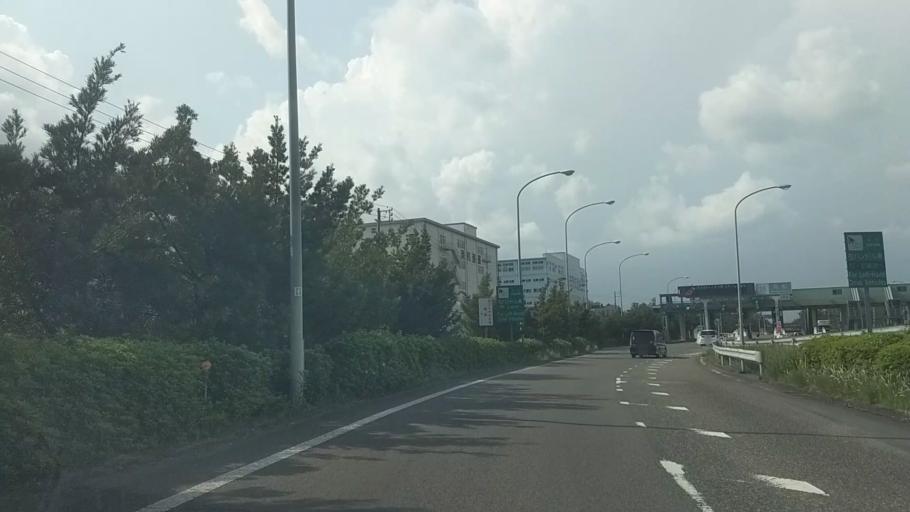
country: JP
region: Shizuoka
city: Hamakita
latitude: 34.7436
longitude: 137.7888
